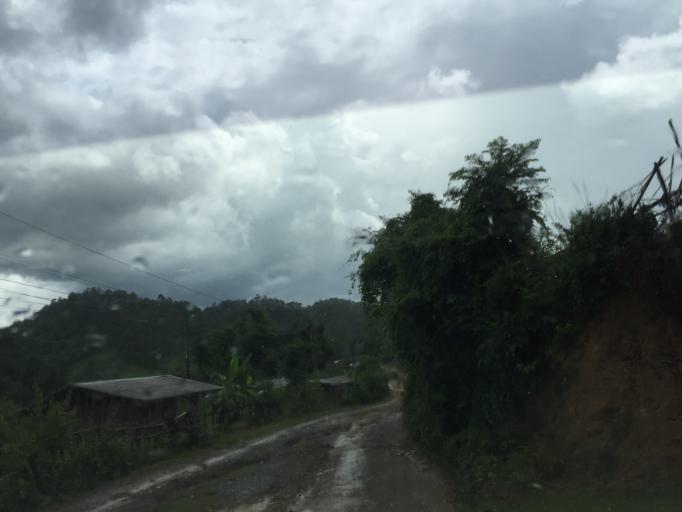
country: LA
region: Xiangkhoang
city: Muang Phonsavan
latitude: 19.3398
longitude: 103.5755
